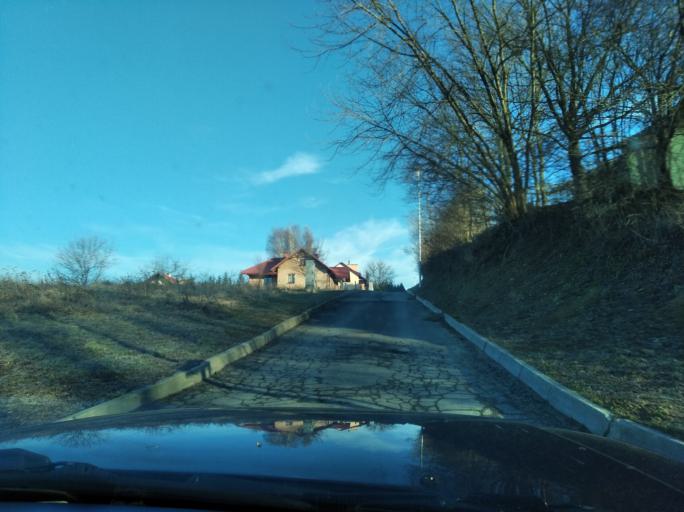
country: PL
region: Subcarpathian Voivodeship
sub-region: Powiat strzyzowski
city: Strzyzow
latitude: 49.8724
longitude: 21.8050
